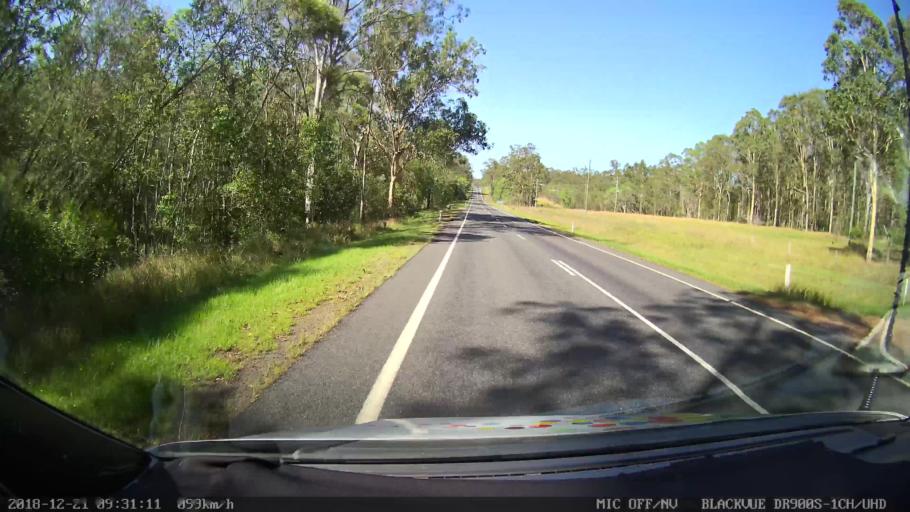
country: AU
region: New South Wales
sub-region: Clarence Valley
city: Maclean
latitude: -29.4570
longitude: 152.9917
